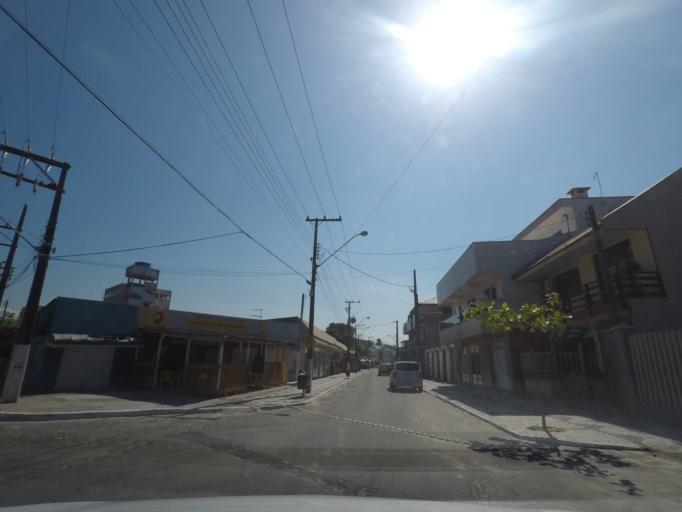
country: BR
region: Parana
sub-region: Guaratuba
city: Guaratuba
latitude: -25.8191
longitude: -48.5309
